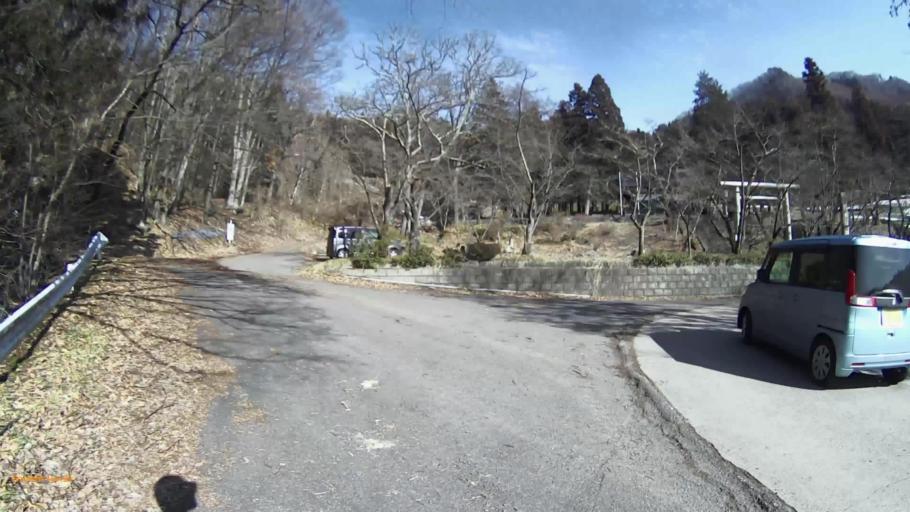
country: JP
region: Nagano
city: Nakano
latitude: 36.7467
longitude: 138.3832
